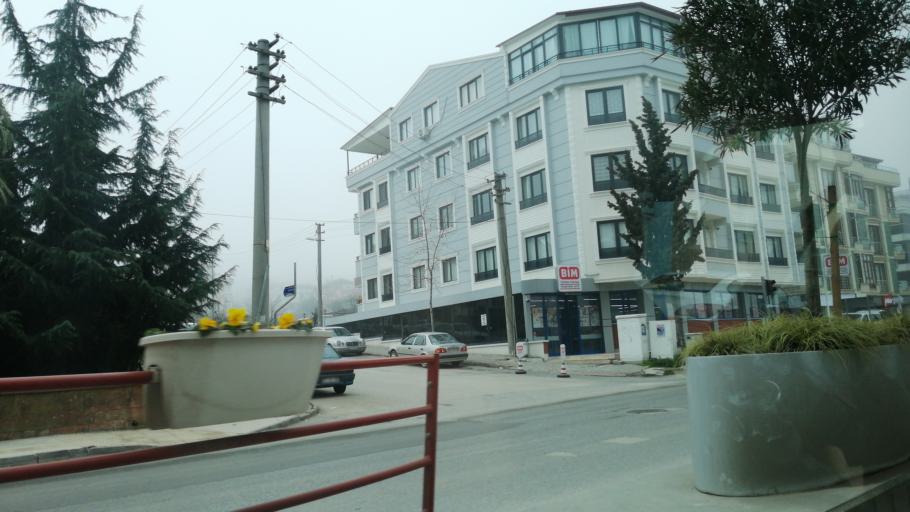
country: TR
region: Yalova
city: Yalova
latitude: 40.6546
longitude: 29.2513
